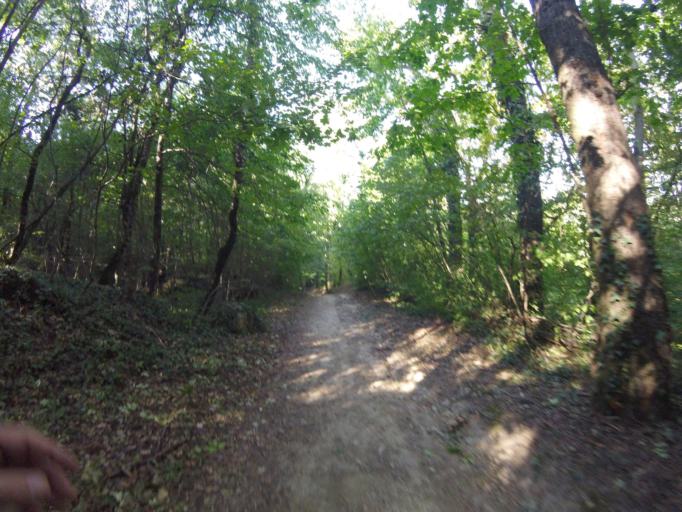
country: HU
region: Pest
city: Budakeszi
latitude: 47.5327
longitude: 18.9646
